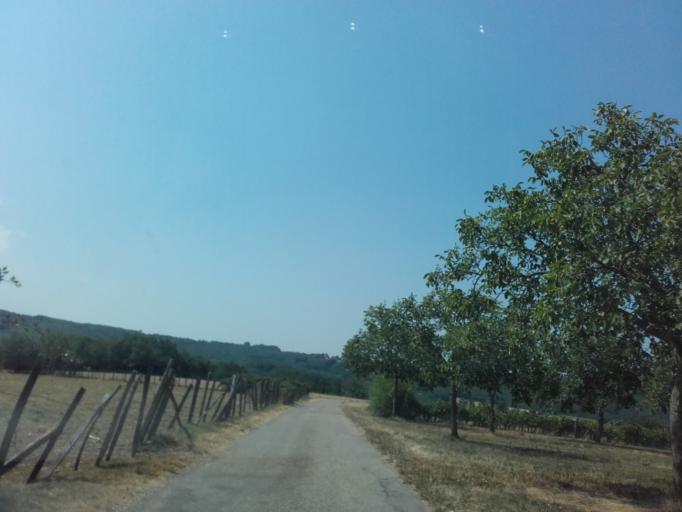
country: FR
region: Rhone-Alpes
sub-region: Departement de l'Isere
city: Saint-Simeon-de-Bressieux
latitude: 45.3187
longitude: 5.2583
